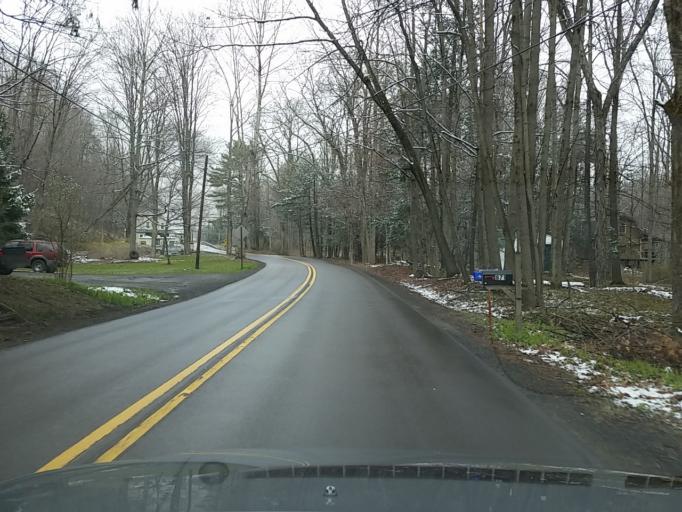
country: US
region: Pennsylvania
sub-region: Sullivan County
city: Laporte
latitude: 41.2896
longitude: -76.3715
